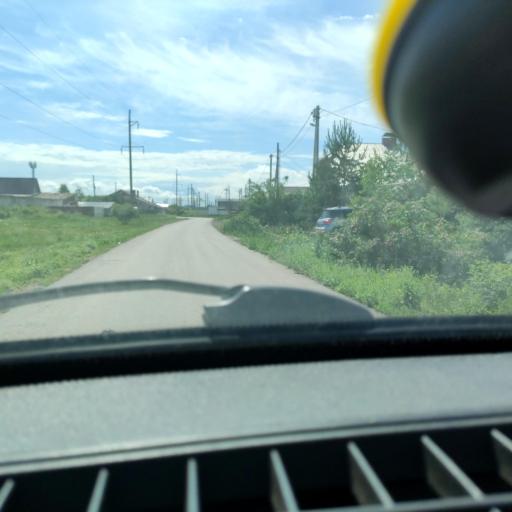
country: RU
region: Samara
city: Zhigulevsk
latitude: 53.5513
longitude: 49.5230
